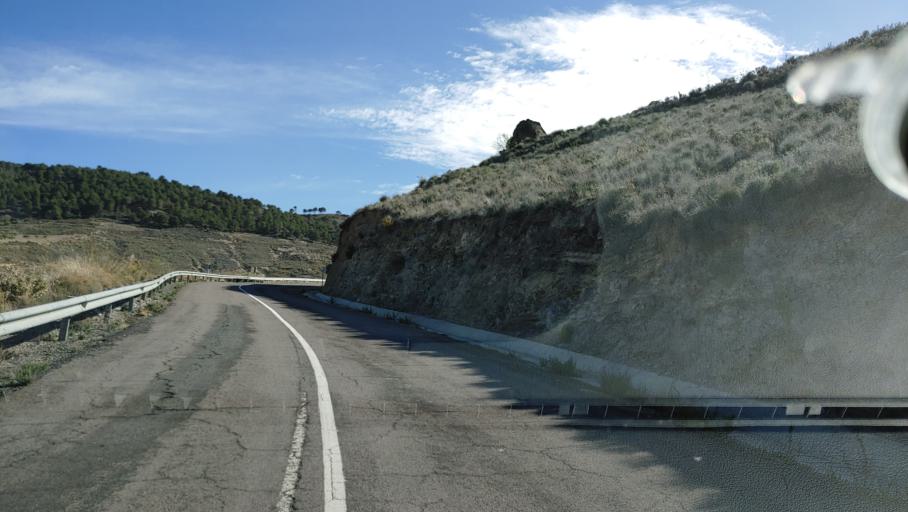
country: ES
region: Andalusia
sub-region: Provincia de Almeria
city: Alicun
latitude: 36.9336
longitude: -2.6016
